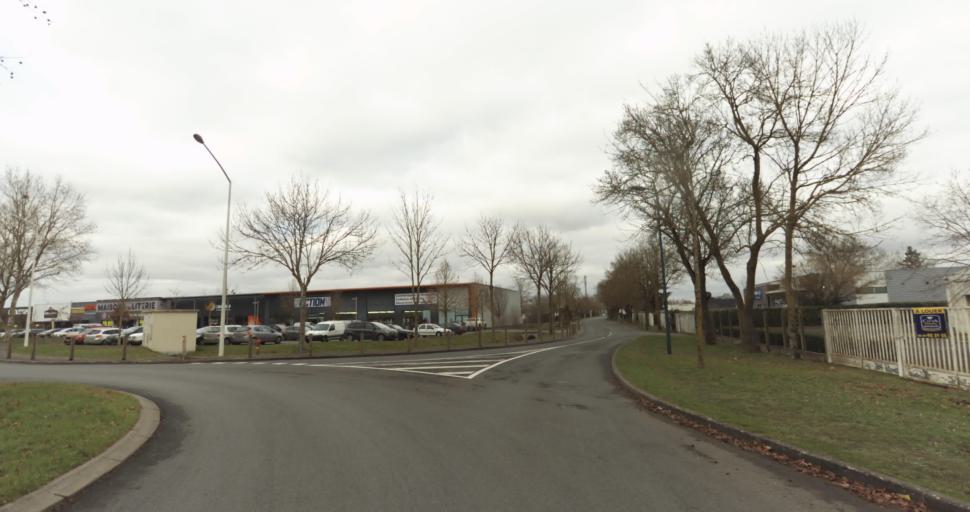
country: FR
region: Pays de la Loire
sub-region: Departement de Maine-et-Loire
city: Saumur
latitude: 47.2768
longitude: -0.0619
